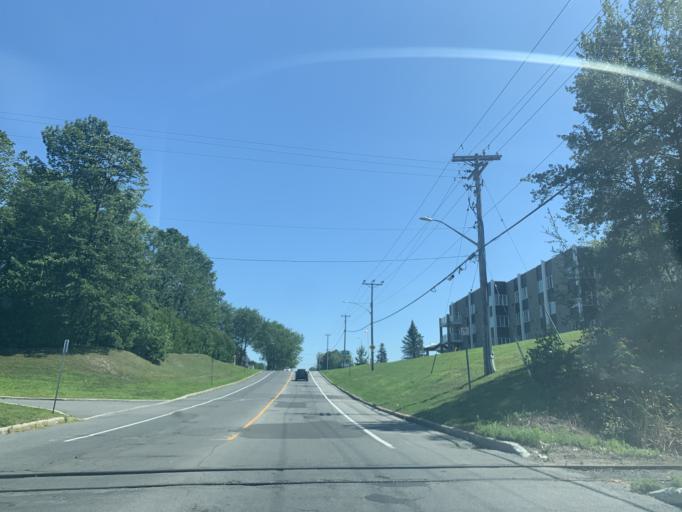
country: CA
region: Ontario
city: Hawkesbury
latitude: 45.5994
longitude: -74.6150
